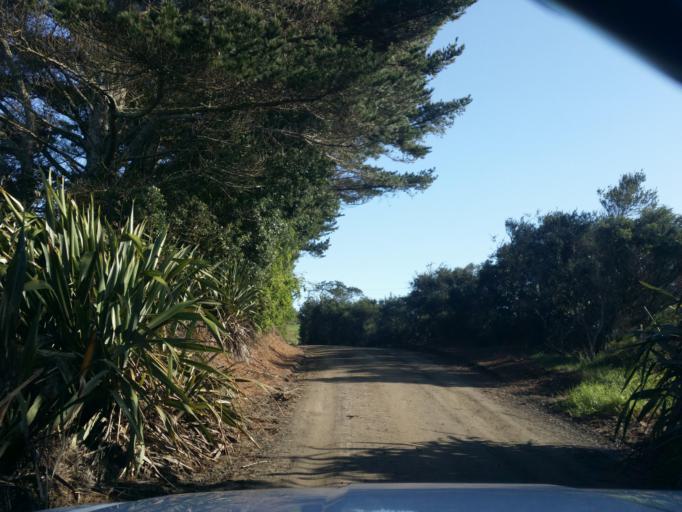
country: NZ
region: Northland
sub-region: Kaipara District
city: Dargaville
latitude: -35.9183
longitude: 173.7321
